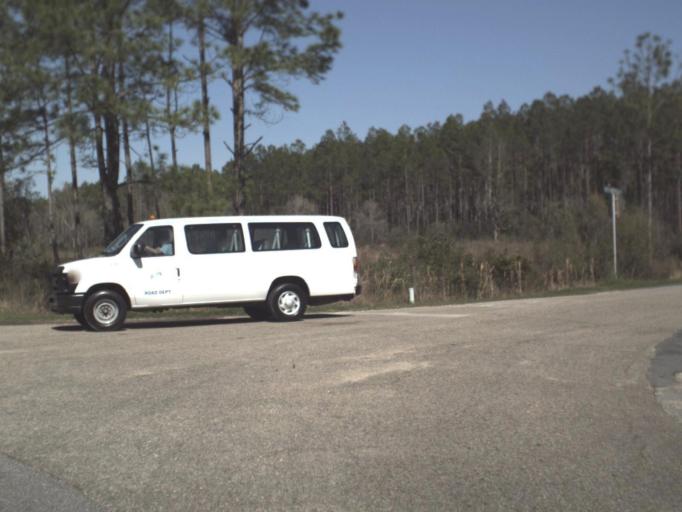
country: US
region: Florida
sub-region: Gulf County
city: Port Saint Joe
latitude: 29.9102
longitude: -85.2052
